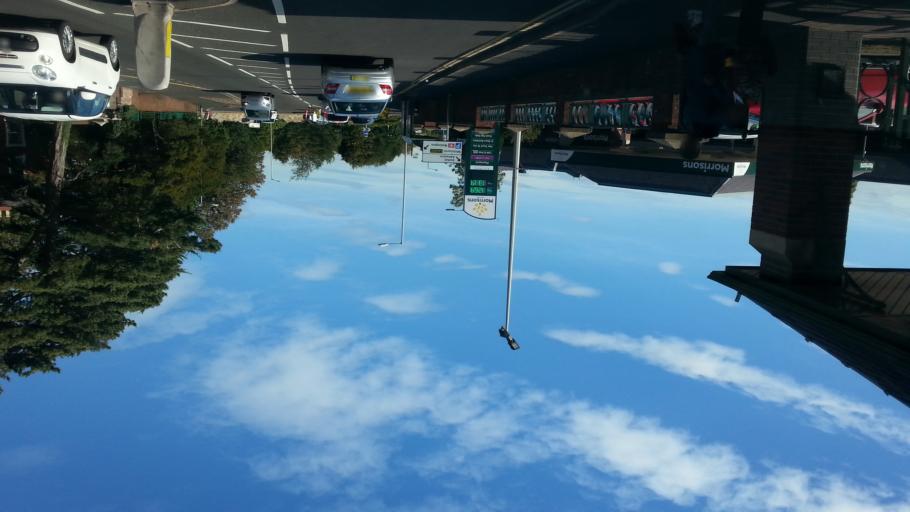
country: GB
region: England
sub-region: Telford and Wrekin
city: Wellington
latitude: 52.7023
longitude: -2.5226
